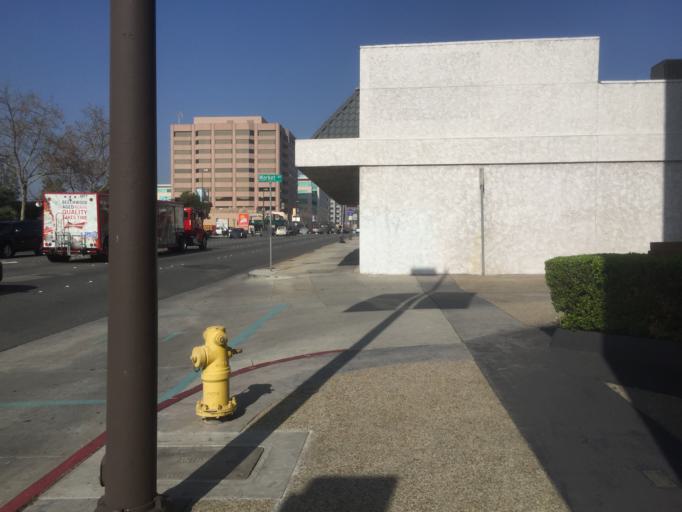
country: US
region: California
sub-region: Los Angeles County
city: Pasadena
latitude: 34.1464
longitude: -118.1321
